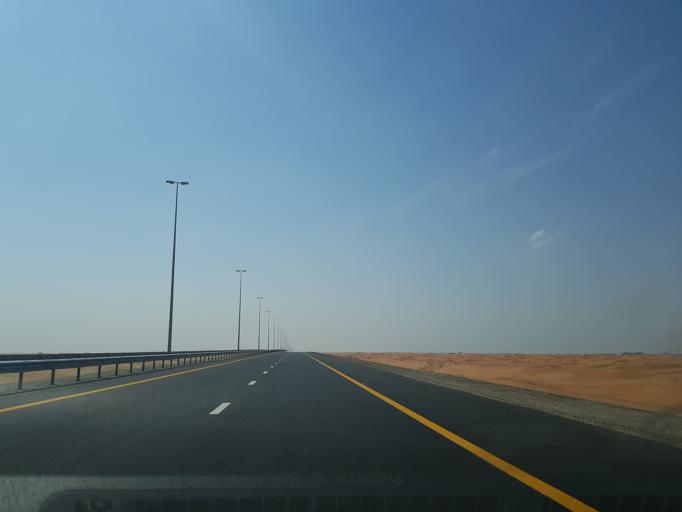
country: AE
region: Ash Shariqah
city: Adh Dhayd
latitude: 25.2533
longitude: 55.7641
